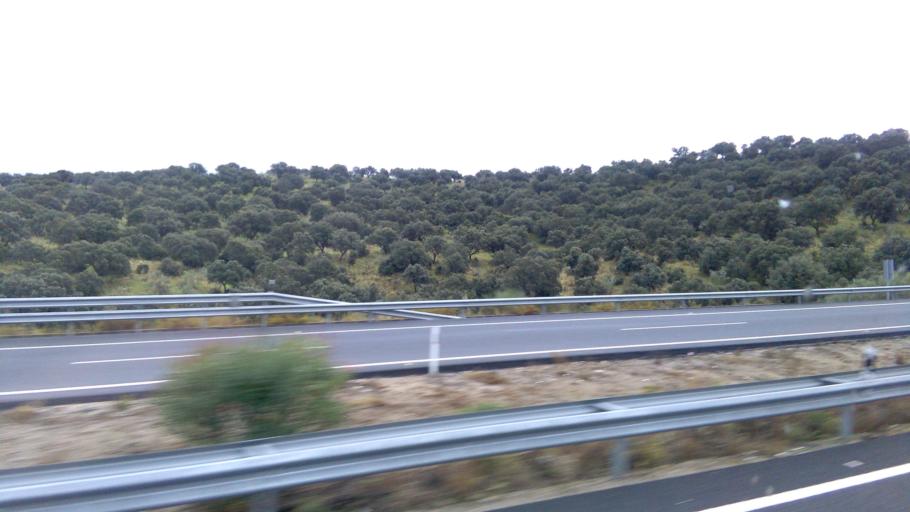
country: ES
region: Extremadura
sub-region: Provincia de Caceres
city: Almaraz
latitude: 39.8036
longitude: -5.6731
